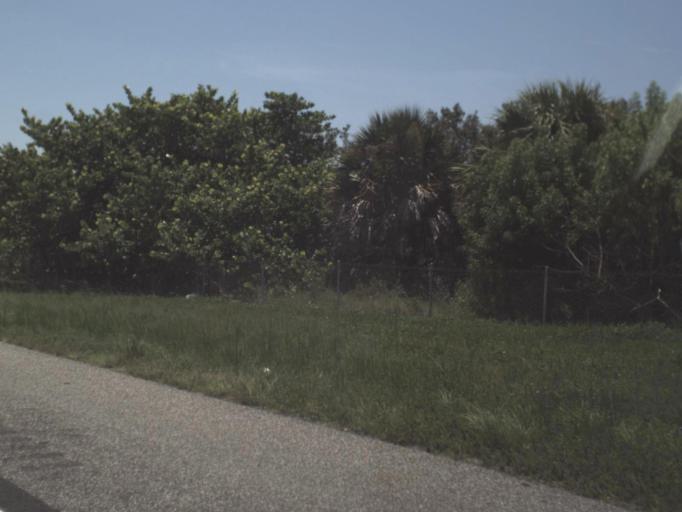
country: US
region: Florida
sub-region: Pinellas County
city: Tierra Verde
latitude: 27.6683
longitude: -82.6777
